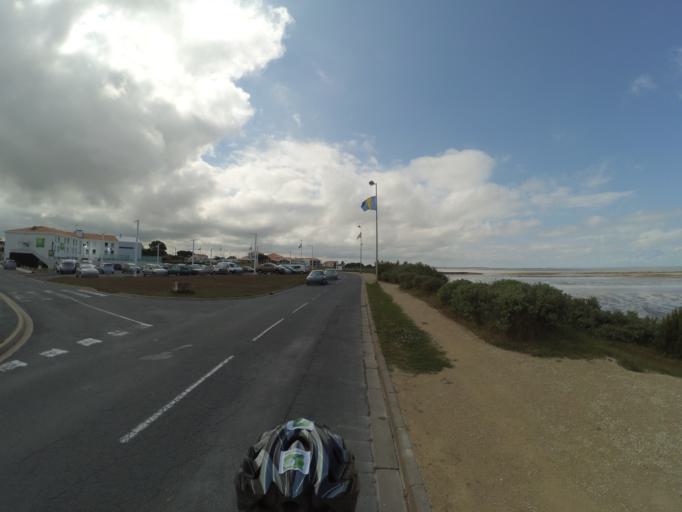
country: FR
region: Poitou-Charentes
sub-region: Departement de la Charente-Maritime
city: Chatelaillon-Plage
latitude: 46.0600
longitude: -1.0898
